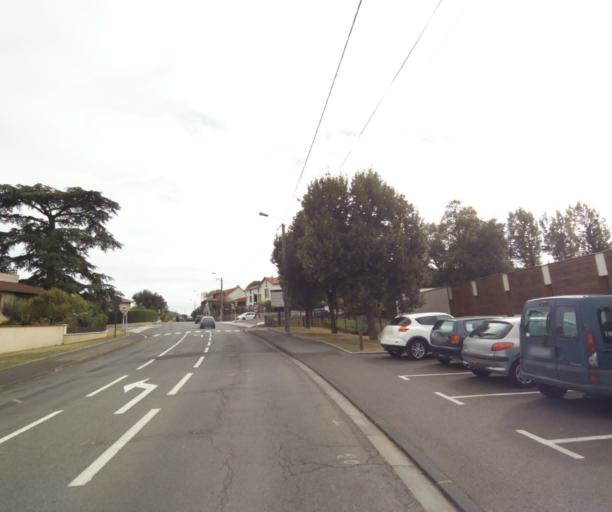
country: FR
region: Auvergne
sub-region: Departement du Puy-de-Dome
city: Le Cendre
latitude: 45.7196
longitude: 3.1883
